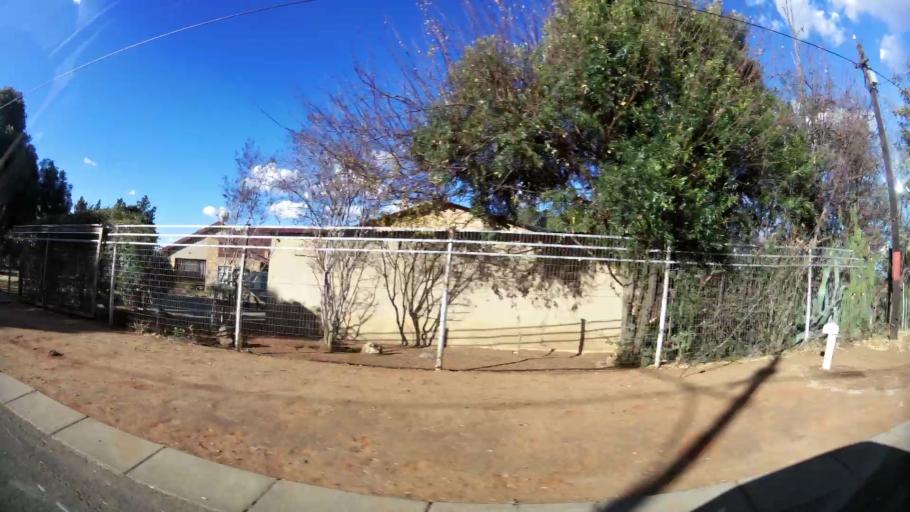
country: ZA
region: North-West
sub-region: Dr Kenneth Kaunda District Municipality
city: Klerksdorp
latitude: -26.8370
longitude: 26.6623
